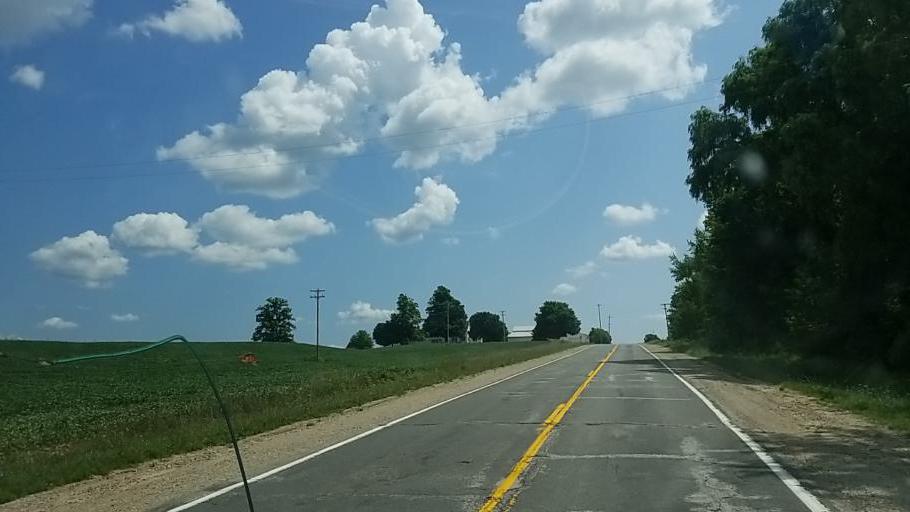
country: US
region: Michigan
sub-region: Kent County
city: Walker
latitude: 43.0737
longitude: -85.7514
